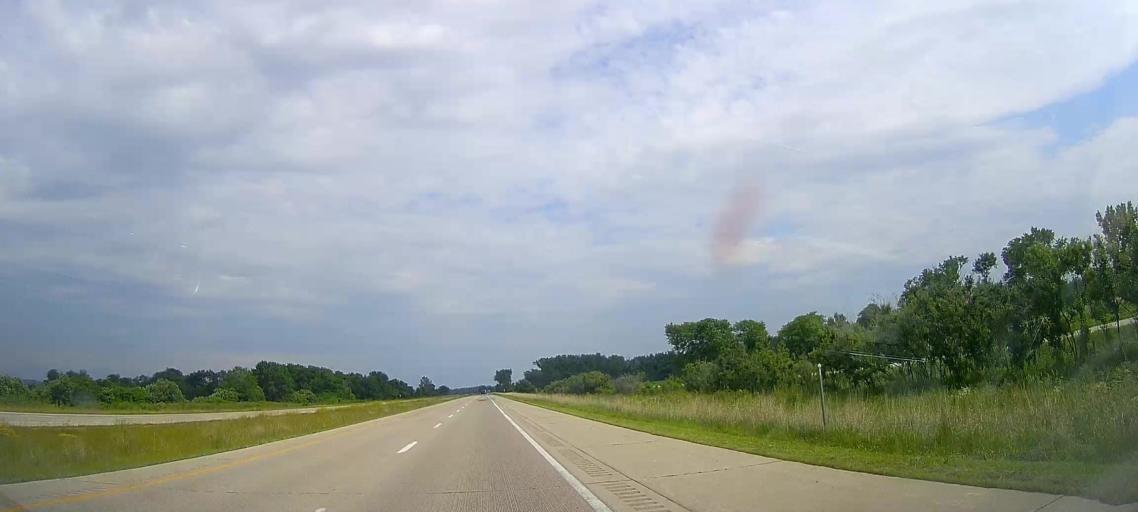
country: US
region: Nebraska
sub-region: Burt County
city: Tekamah
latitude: 41.8438
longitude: -96.0925
